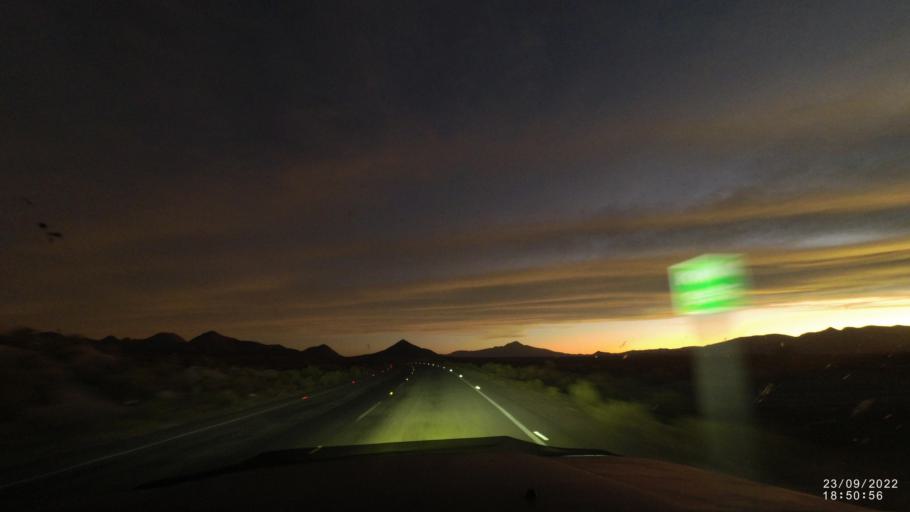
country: BO
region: Oruro
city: Challapata
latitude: -19.4686
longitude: -67.4277
